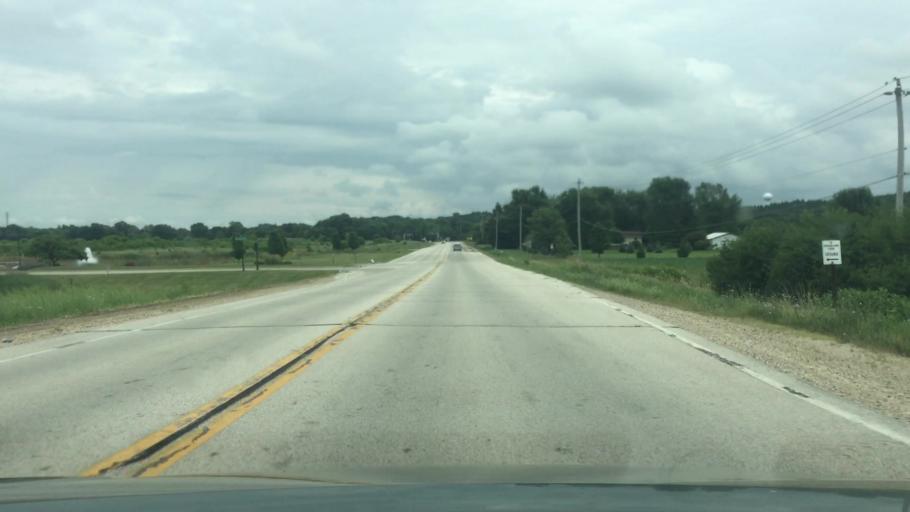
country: US
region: Wisconsin
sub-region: Waukesha County
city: North Prairie
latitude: 42.9300
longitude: -88.4200
